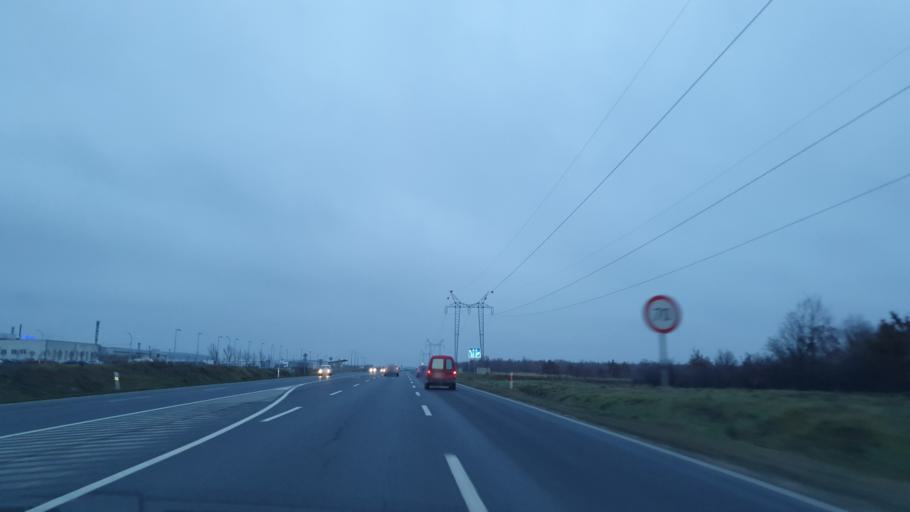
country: HU
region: Veszprem
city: Osi
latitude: 47.1998
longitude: 18.2083
